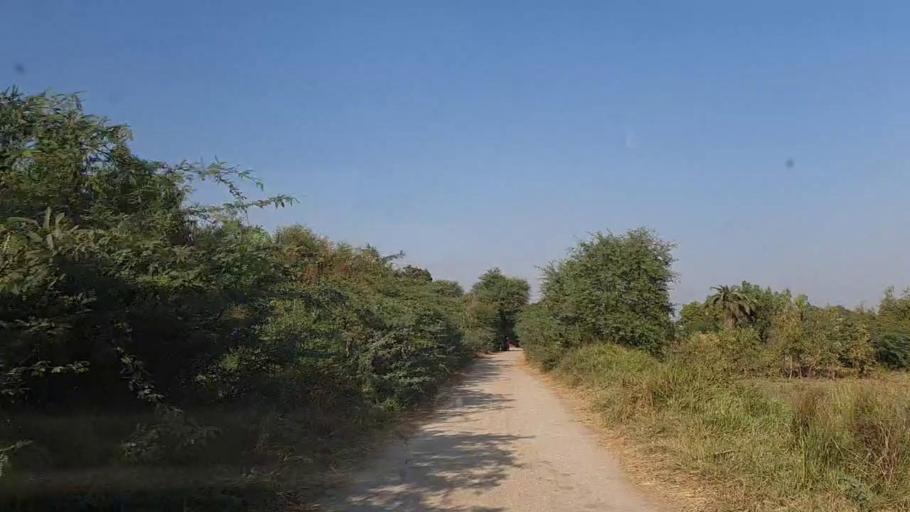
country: PK
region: Sindh
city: Thatta
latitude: 24.7665
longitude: 67.9662
